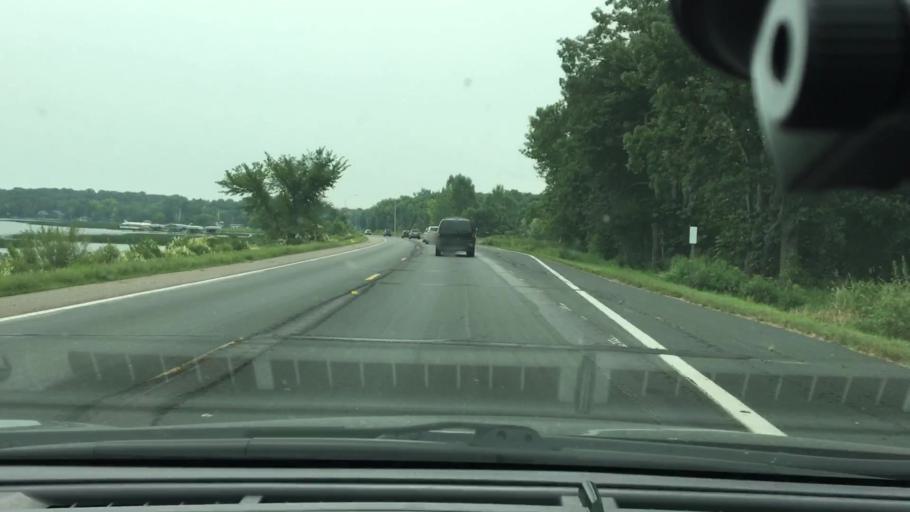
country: US
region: Minnesota
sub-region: Mille Lacs County
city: Vineland
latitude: 46.2556
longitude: -93.8218
